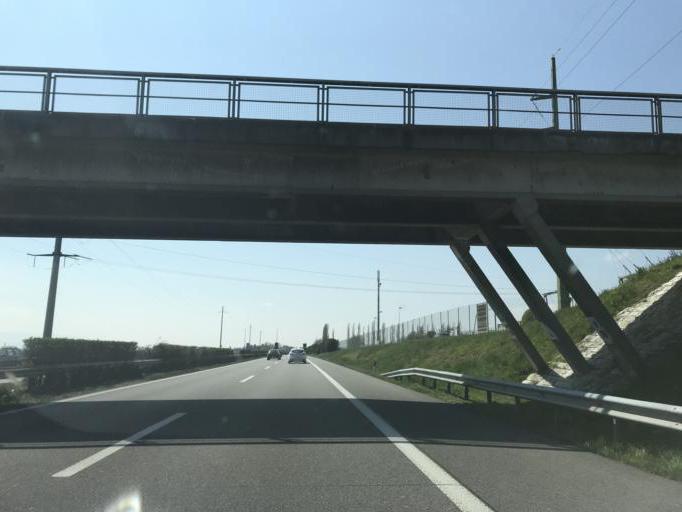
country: CH
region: Vaud
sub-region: Nyon District
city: Founex
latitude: 46.3482
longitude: 6.1702
